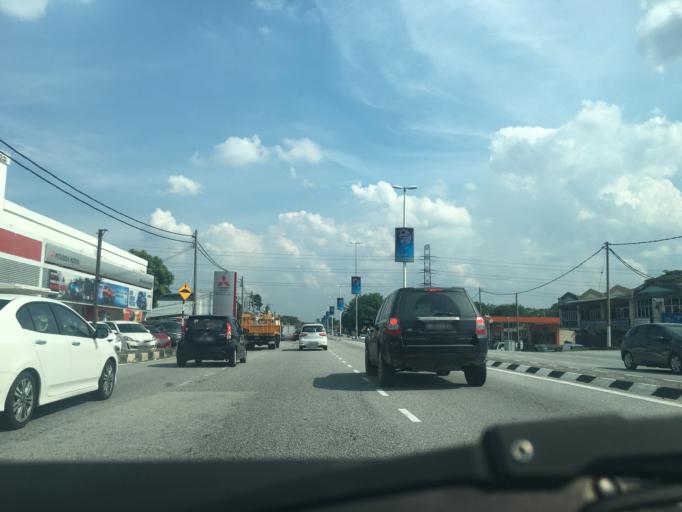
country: MY
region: Perak
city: Ipoh
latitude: 4.6219
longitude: 101.0810
